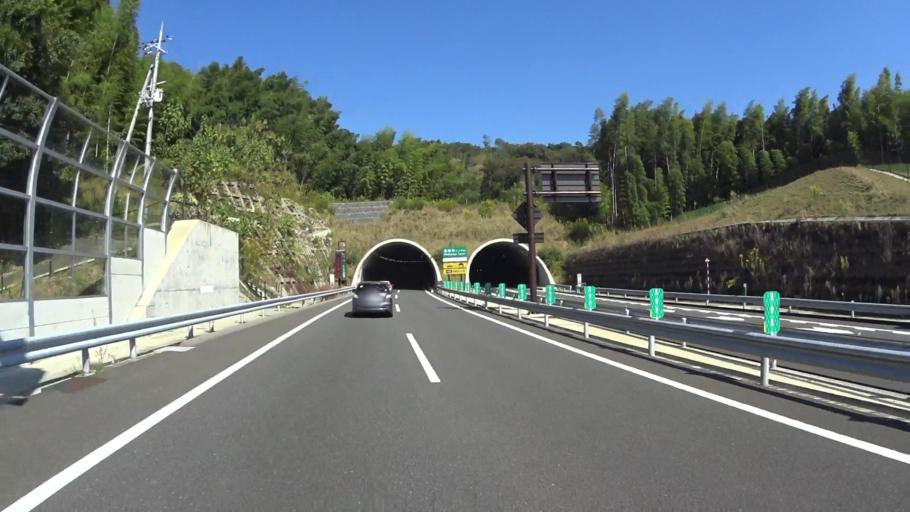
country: JP
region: Kyoto
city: Muko
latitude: 34.9579
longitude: 135.6533
